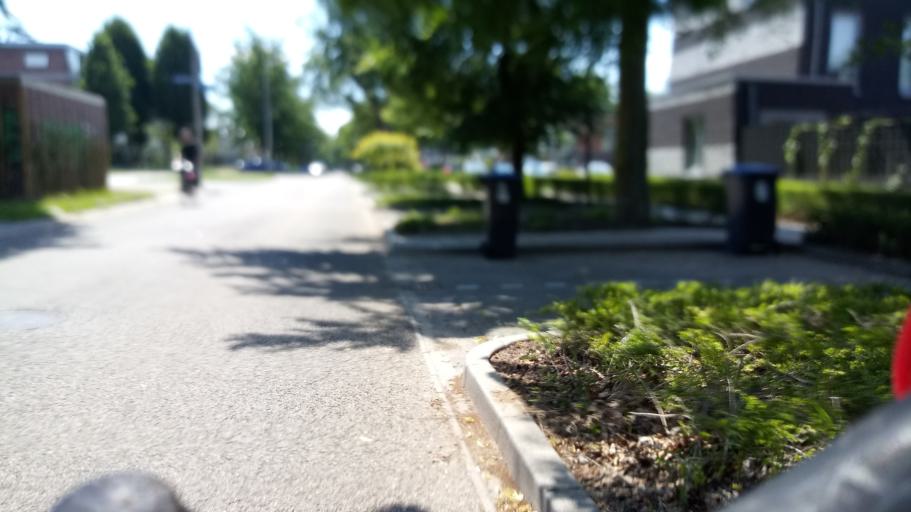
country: NL
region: Gelderland
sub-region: Gemeente Nijmegen
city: Nijmegen
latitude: 51.8144
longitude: 5.8405
